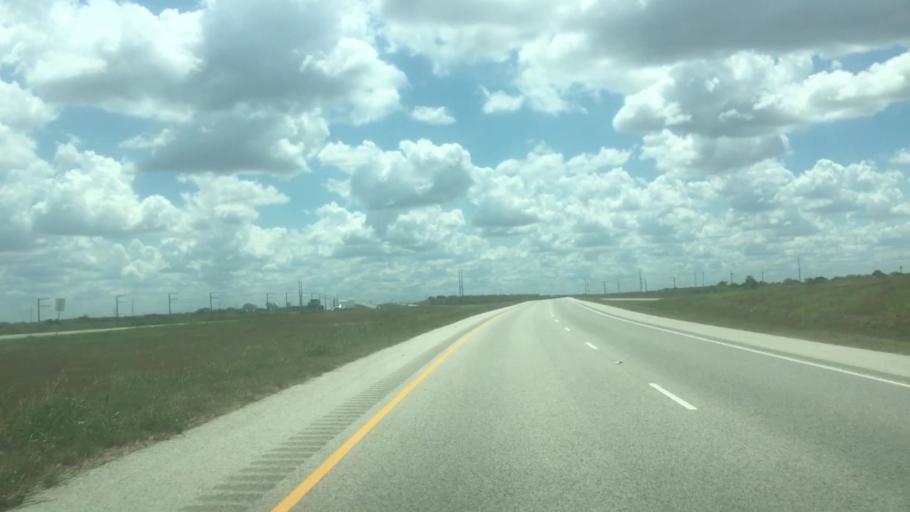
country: US
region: Texas
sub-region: Caldwell County
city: Uhland
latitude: 30.0198
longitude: -97.6876
